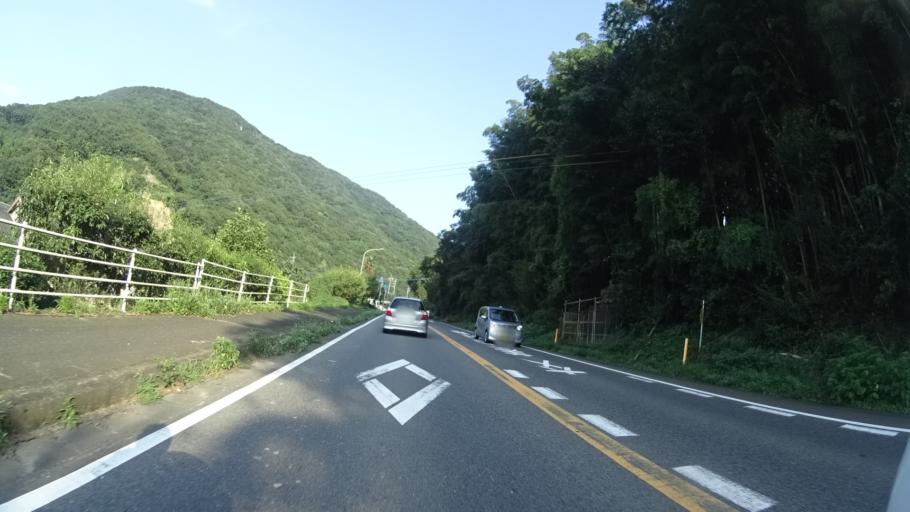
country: JP
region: Oita
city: Bungo-Takada-shi
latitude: 33.4905
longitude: 131.3296
